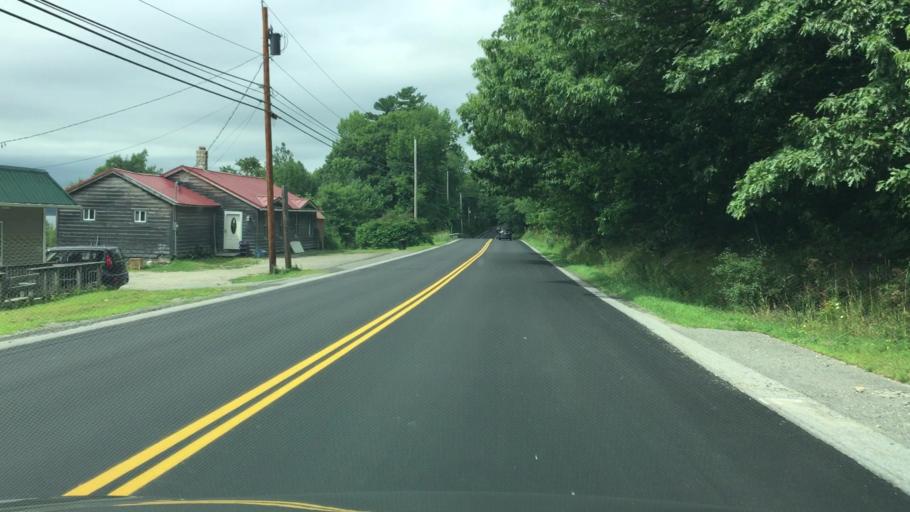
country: US
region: Maine
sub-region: Waldo County
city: Winterport
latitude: 44.6102
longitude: -68.8222
